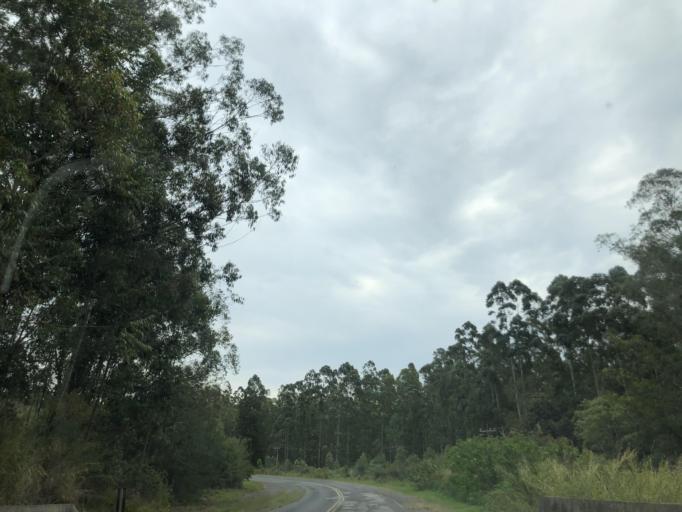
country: BR
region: Sao Paulo
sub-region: Pilar Do Sul
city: Pilar do Sul
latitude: -23.8121
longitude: -47.6431
